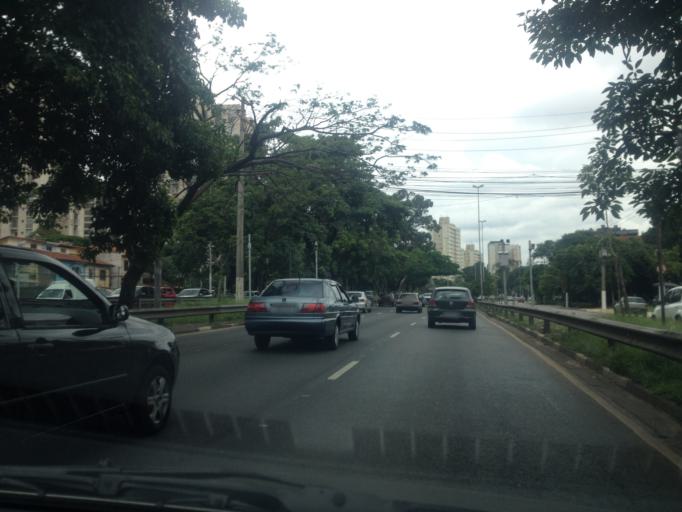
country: BR
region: Sao Paulo
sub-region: Sao Paulo
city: Sao Paulo
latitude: -23.5992
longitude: -46.6862
